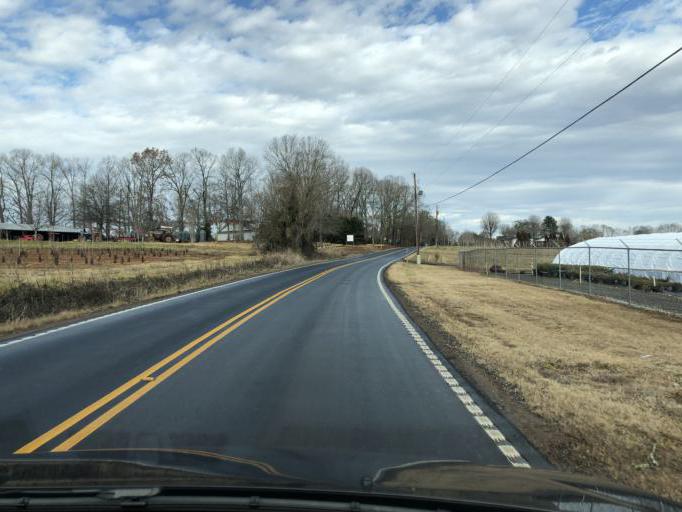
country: US
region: South Carolina
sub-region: Greenville County
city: Five Forks
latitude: 34.8598
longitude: -82.1986
